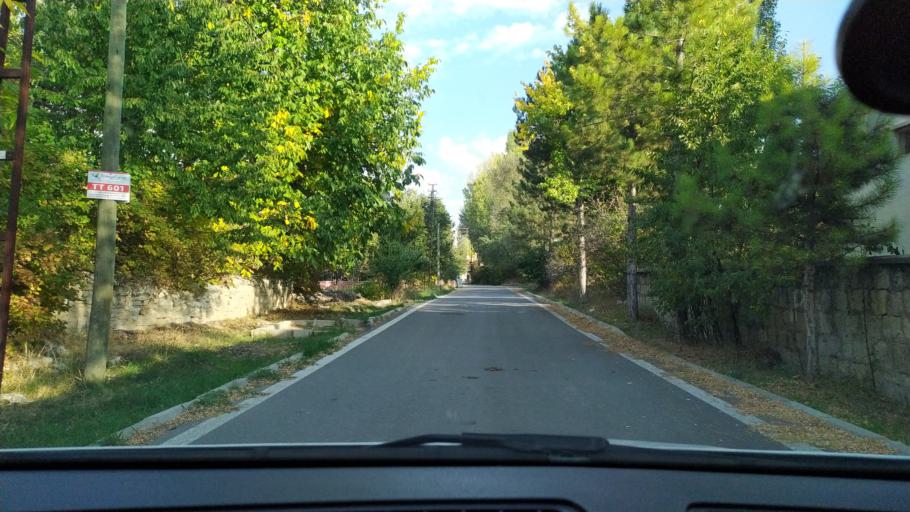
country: TR
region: Kayseri
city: Akkisla
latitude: 39.0007
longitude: 36.1701
